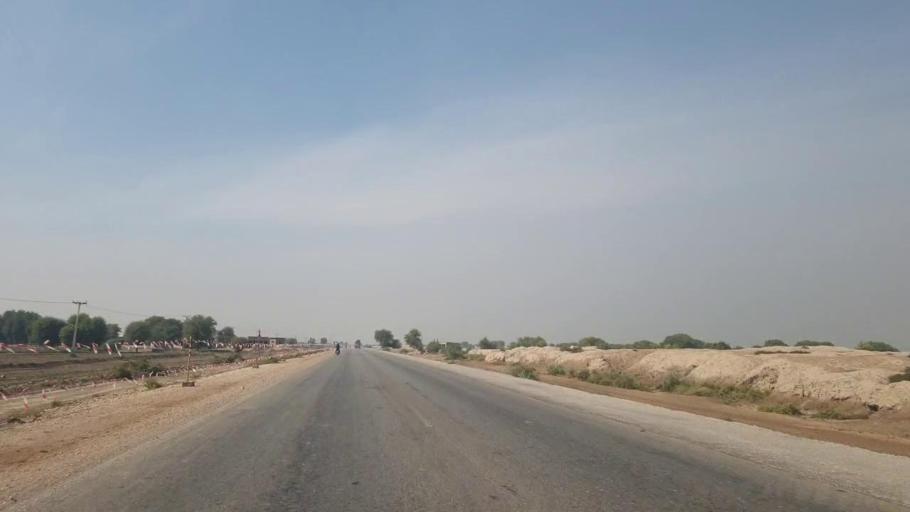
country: PK
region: Sindh
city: Sann
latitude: 25.9884
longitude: 68.1784
